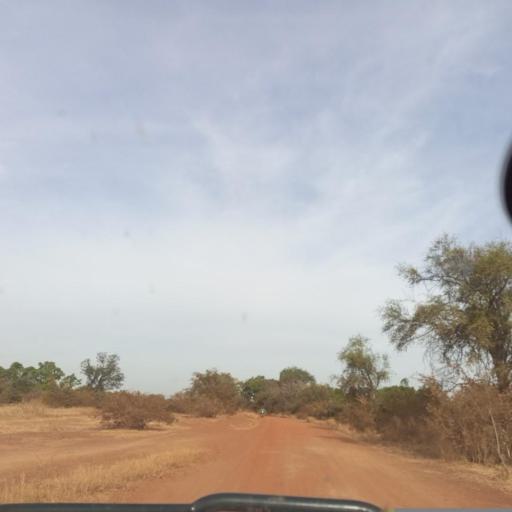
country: ML
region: Koulikoro
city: Koulikoro
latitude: 13.1048
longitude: -7.6445
